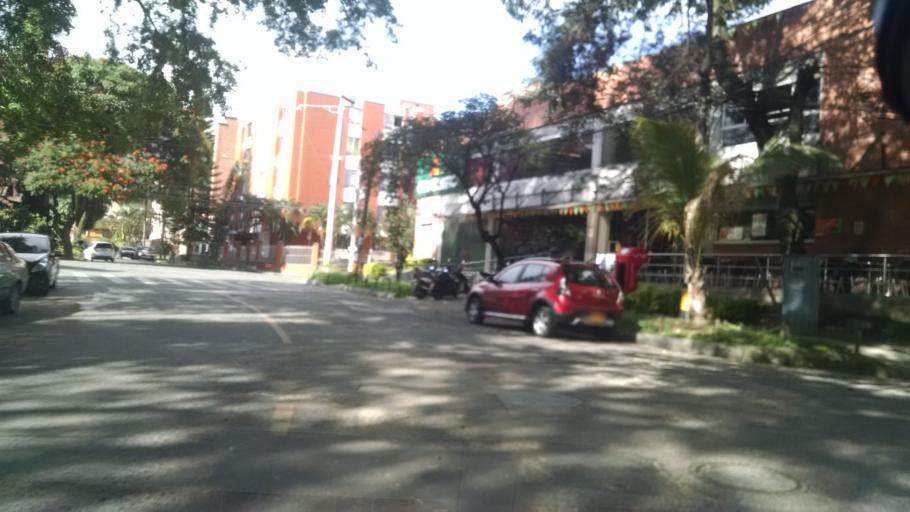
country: CO
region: Antioquia
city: Medellin
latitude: 6.2558
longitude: -75.6011
